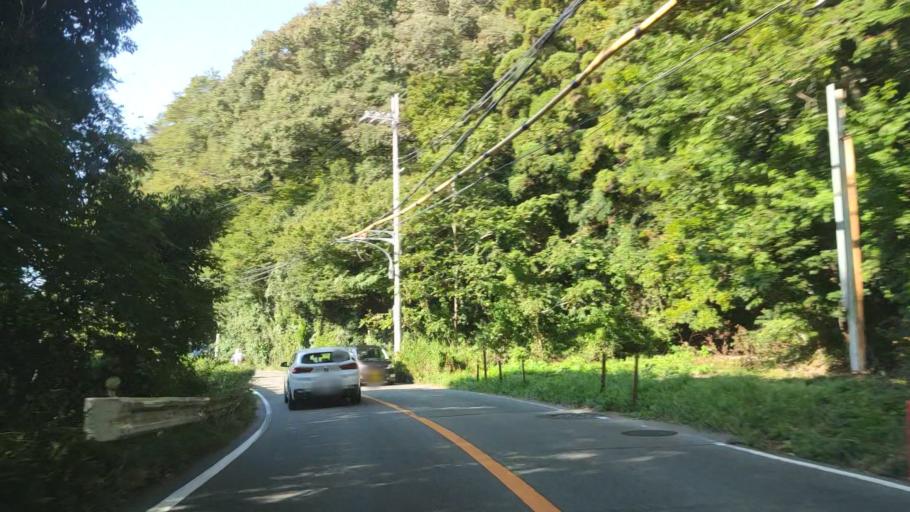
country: JP
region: Hyogo
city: Sandacho
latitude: 34.7920
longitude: 135.2120
